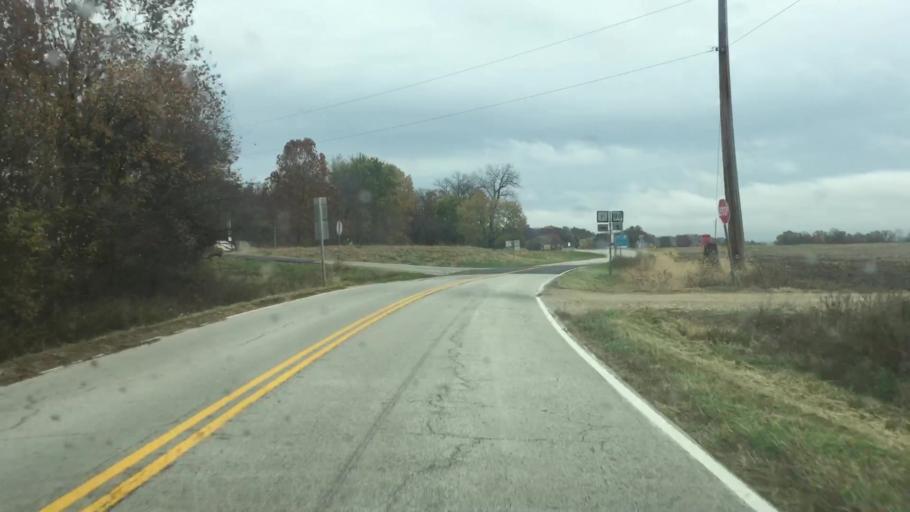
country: US
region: Missouri
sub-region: Gasconade County
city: Hermann
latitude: 38.7131
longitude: -91.5325
